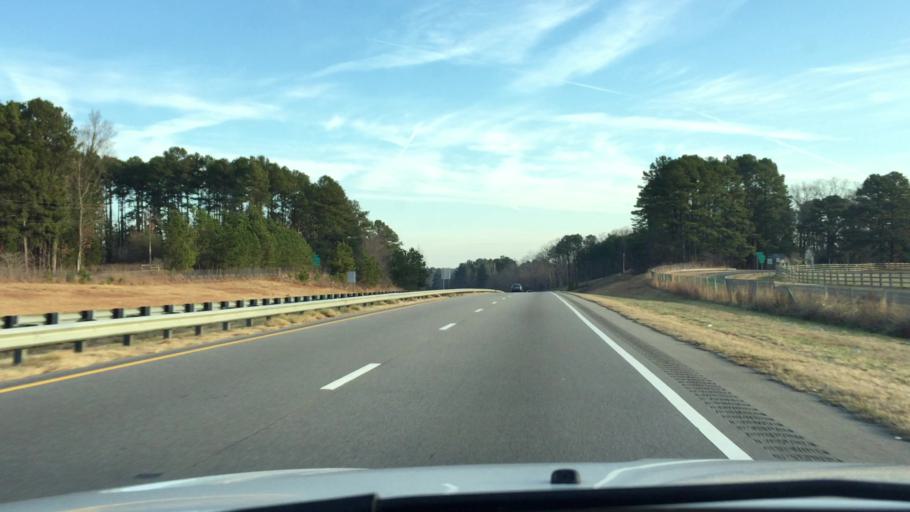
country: US
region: North Carolina
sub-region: Lee County
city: Sanford
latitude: 35.4587
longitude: -79.2082
